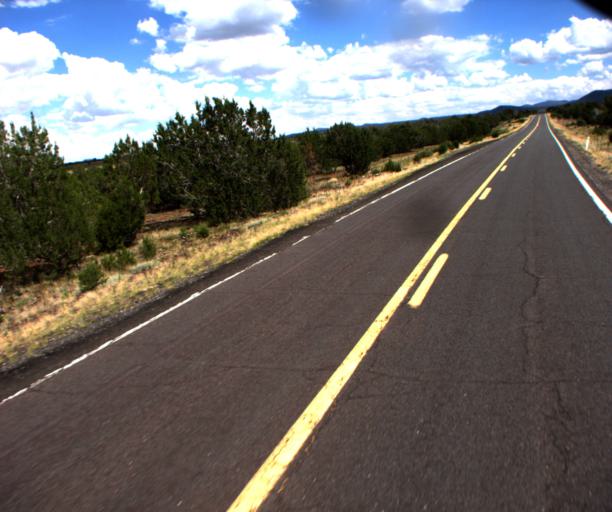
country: US
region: Arizona
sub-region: Coconino County
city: Parks
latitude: 35.5634
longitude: -111.8851
